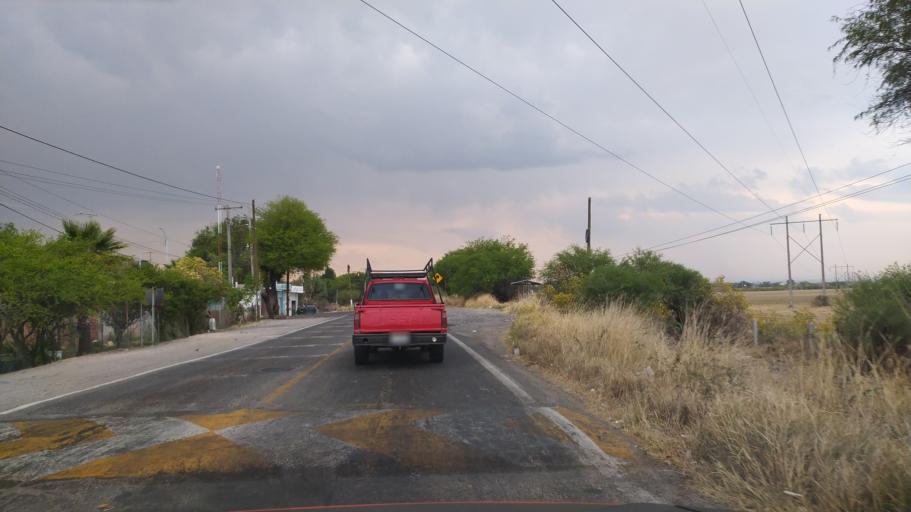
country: MX
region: Guanajuato
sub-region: San Francisco del Rincon
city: San Ignacio de Hidalgo
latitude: 20.8277
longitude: -101.9007
